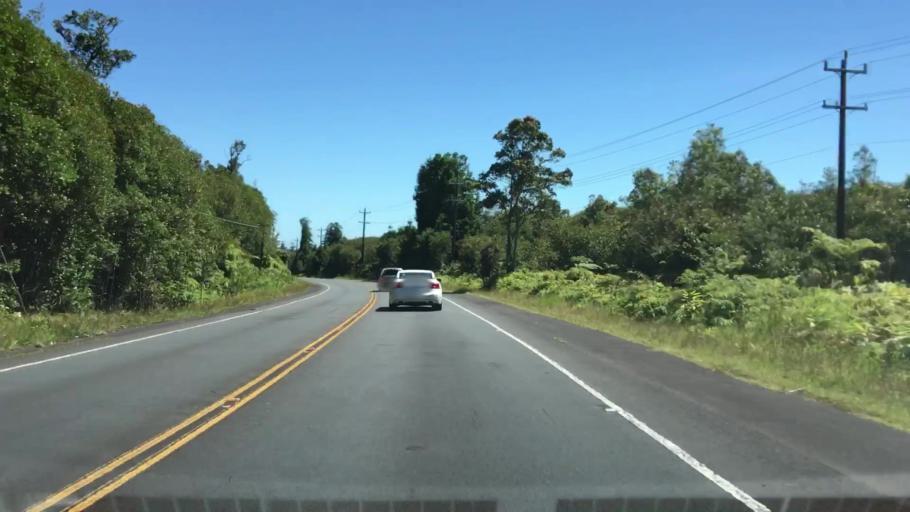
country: US
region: Hawaii
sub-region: Hawaii County
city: Volcano
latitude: 19.4561
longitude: -155.1728
